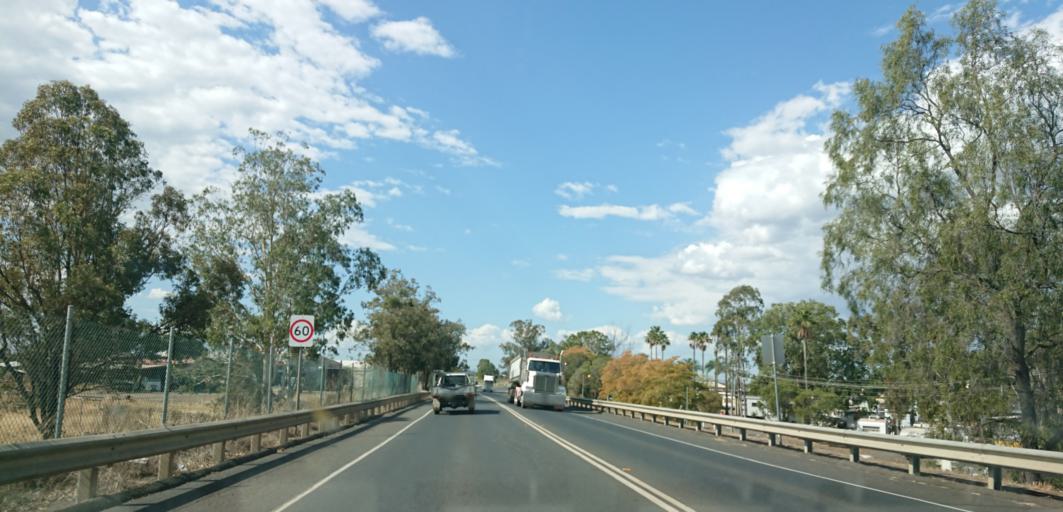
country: AU
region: Queensland
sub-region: Lockyer Valley
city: Gatton
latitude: -27.5562
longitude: 152.2866
